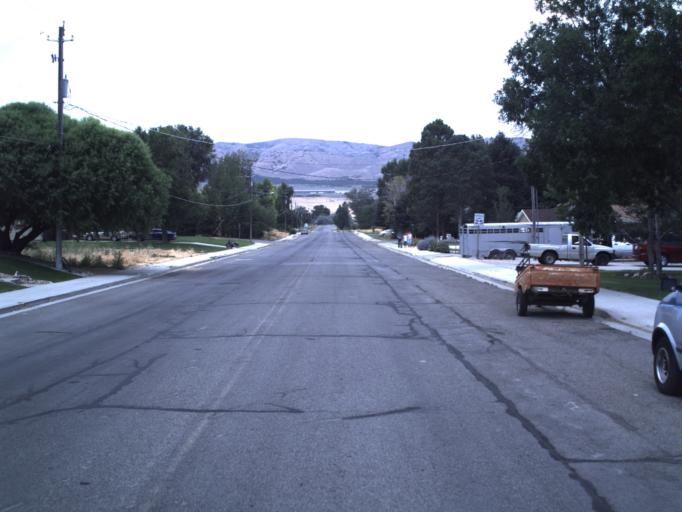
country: US
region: Utah
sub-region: Juab County
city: Mona
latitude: 39.8191
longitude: -111.8557
